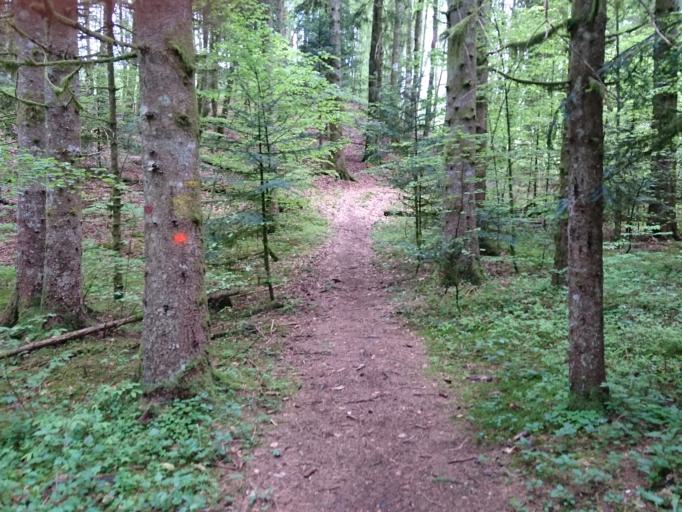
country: FR
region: Rhone-Alpes
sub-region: Departement de l'Ain
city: Oyonnax
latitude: 46.2125
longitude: 5.6904
